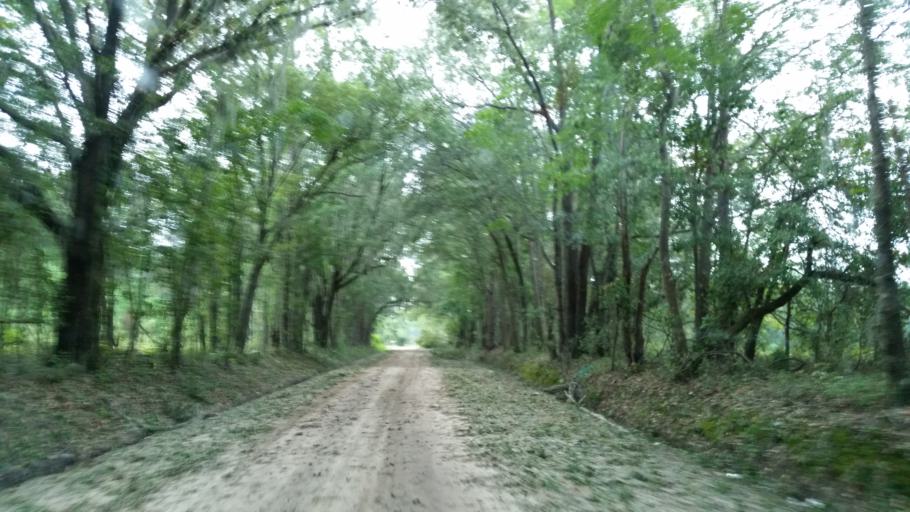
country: US
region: Georgia
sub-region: Lowndes County
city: Valdosta
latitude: 30.7240
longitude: -83.2848
